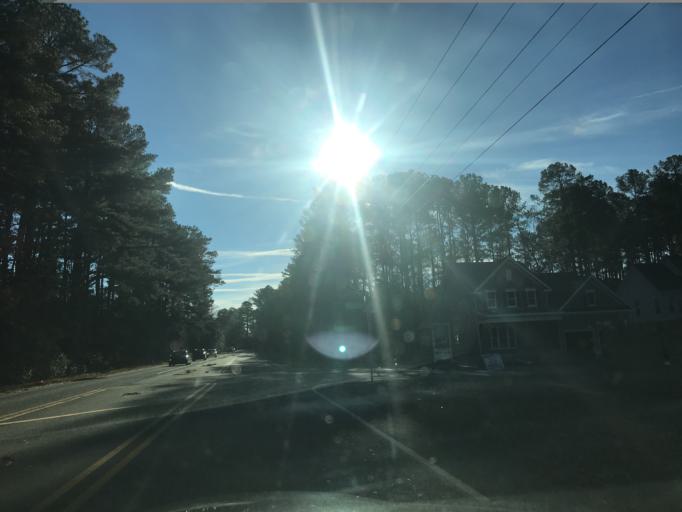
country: US
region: North Carolina
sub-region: Wake County
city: West Raleigh
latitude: 35.9045
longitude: -78.6890
